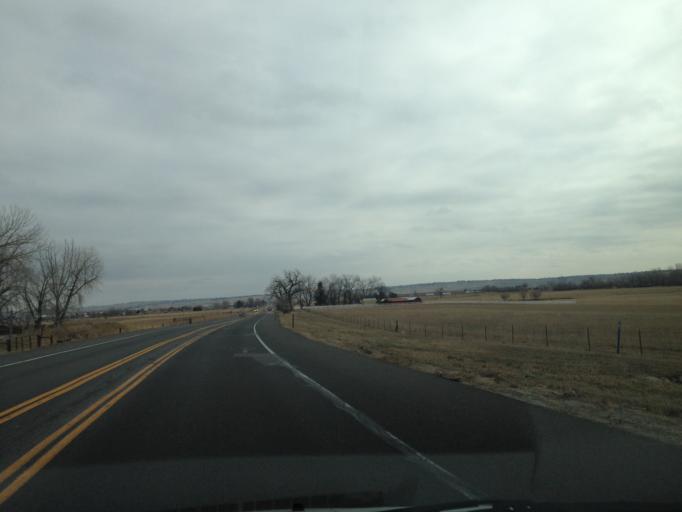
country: US
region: Colorado
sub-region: Boulder County
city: Louisville
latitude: 39.9579
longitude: -105.1427
